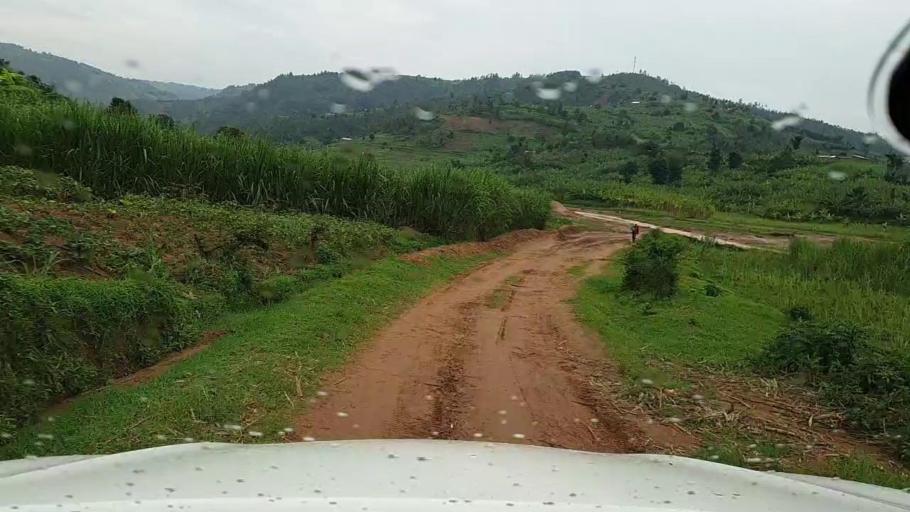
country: RW
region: Kigali
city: Kigali
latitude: -1.8965
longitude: 29.9522
